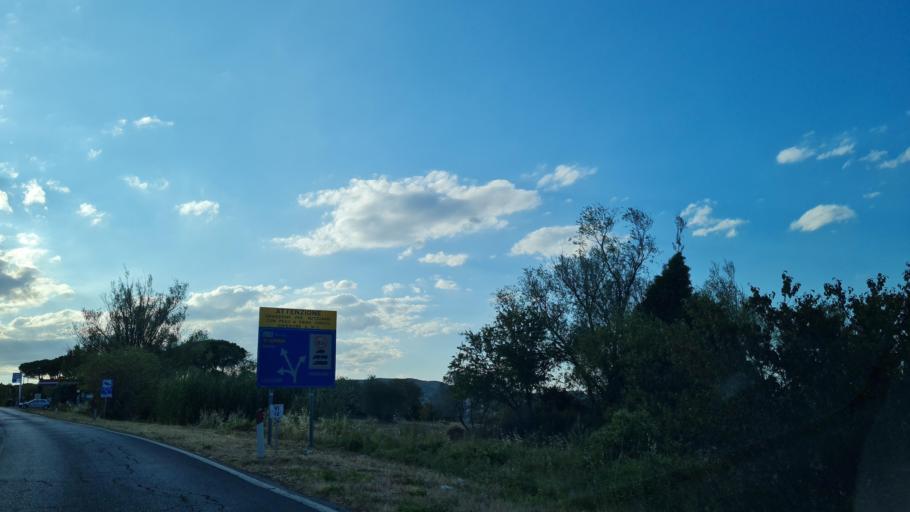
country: IT
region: Tuscany
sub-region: Provincia di Siena
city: Chianciano Terme
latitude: 43.0346
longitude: 11.8425
